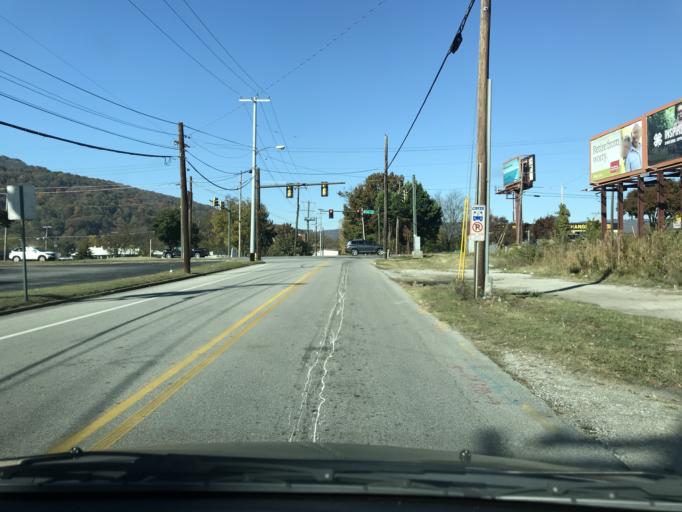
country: US
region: Tennessee
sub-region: Hamilton County
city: Chattanooga
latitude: 35.0174
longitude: -85.3216
